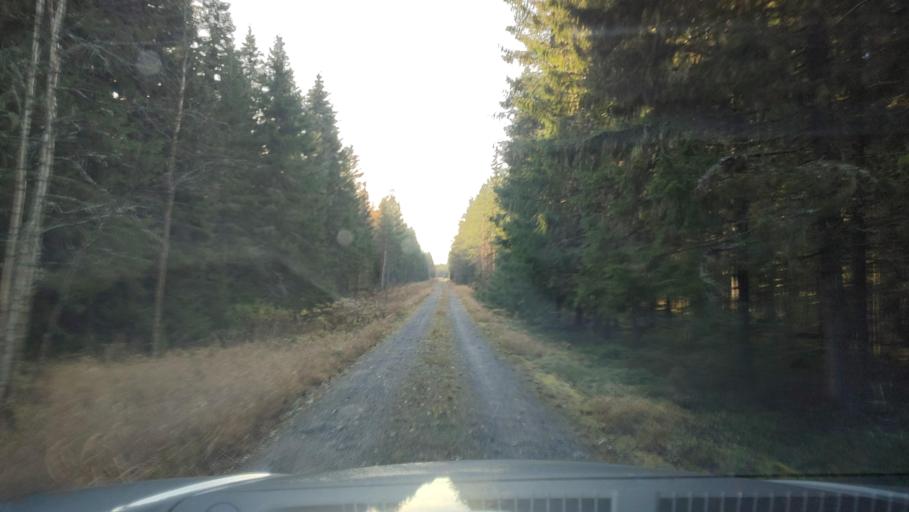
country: FI
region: Southern Ostrobothnia
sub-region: Suupohja
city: Karijoki
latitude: 62.1866
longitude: 21.6077
